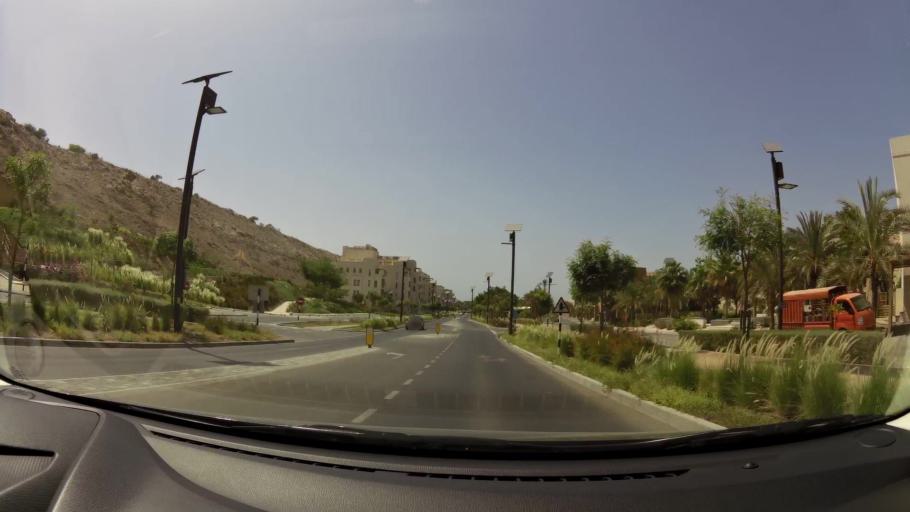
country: OM
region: Muhafazat Masqat
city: Muscat
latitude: 23.6313
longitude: 58.5018
